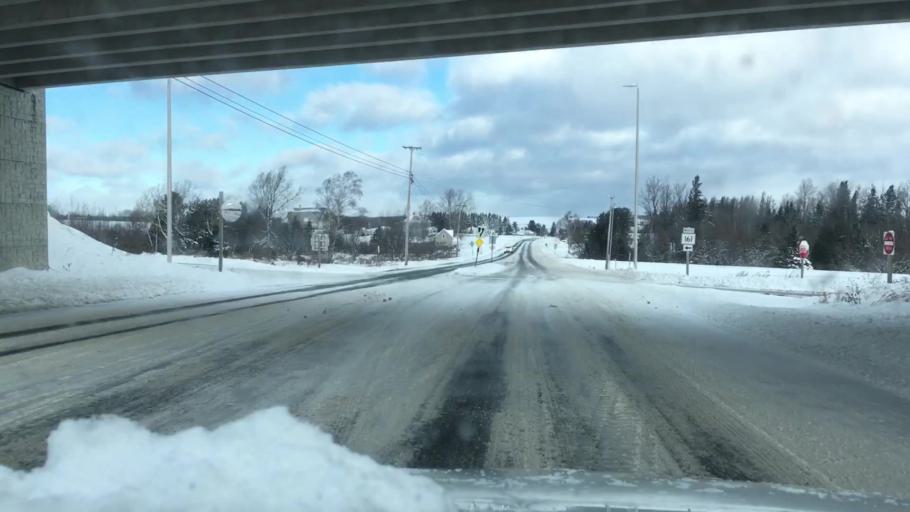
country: US
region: Maine
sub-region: Aroostook County
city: Caribou
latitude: 46.8877
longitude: -68.0142
